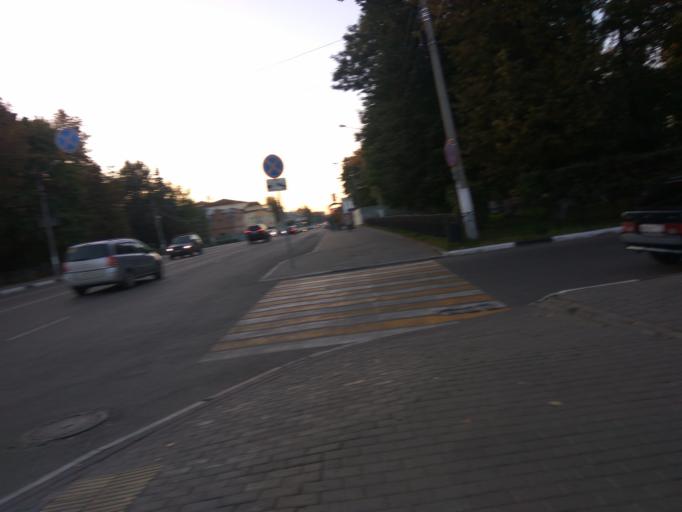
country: RU
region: Moskovskaya
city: Yegor'yevsk
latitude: 55.3825
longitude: 39.0368
